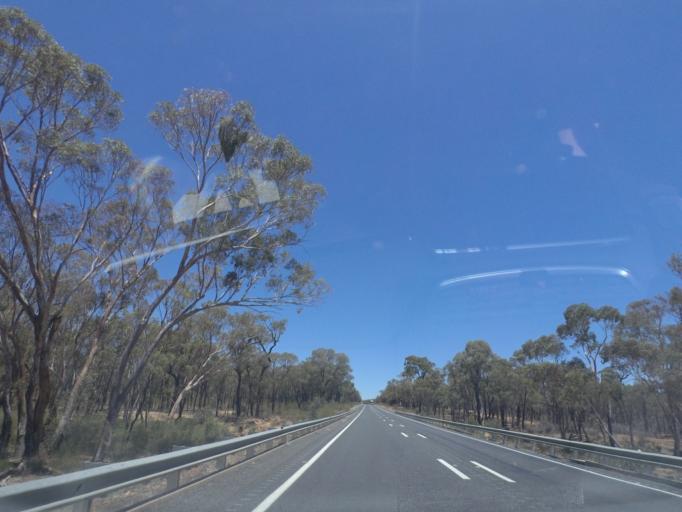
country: AU
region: New South Wales
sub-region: Warrumbungle Shire
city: Coonabarabran
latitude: -30.8810
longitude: 149.4463
